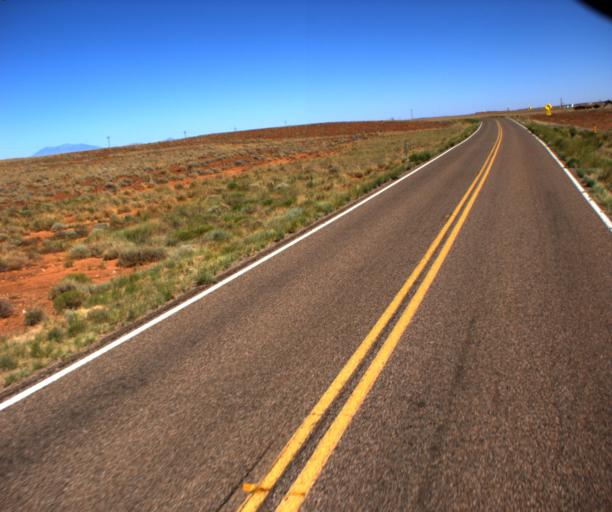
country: US
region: Arizona
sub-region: Coconino County
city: LeChee
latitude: 35.1713
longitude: -110.9178
